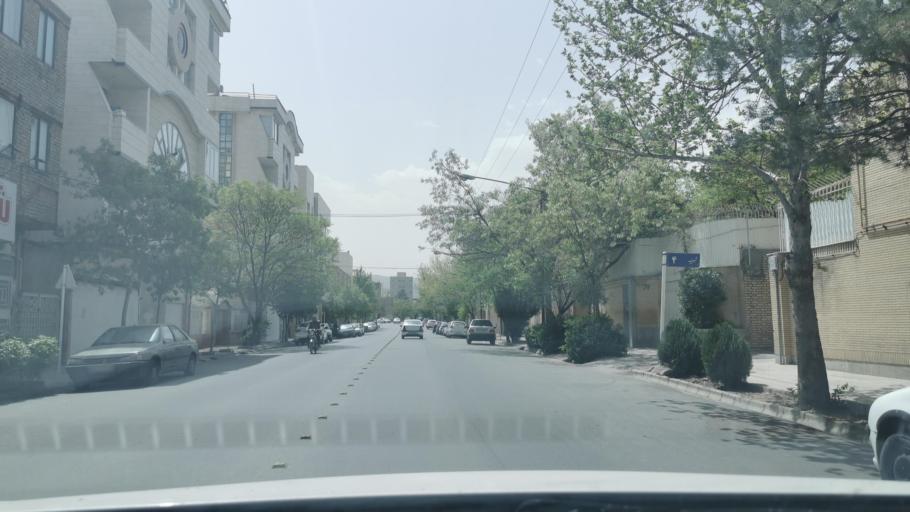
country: IR
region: Razavi Khorasan
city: Mashhad
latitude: 36.3372
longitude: 59.4820
